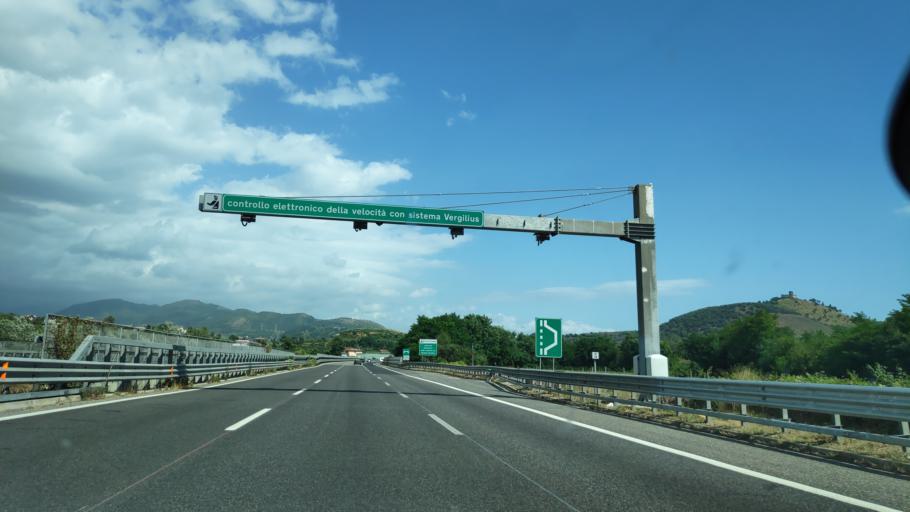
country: IT
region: Campania
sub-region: Provincia di Salerno
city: San Mango Piemonte
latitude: 40.6867
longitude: 14.8472
